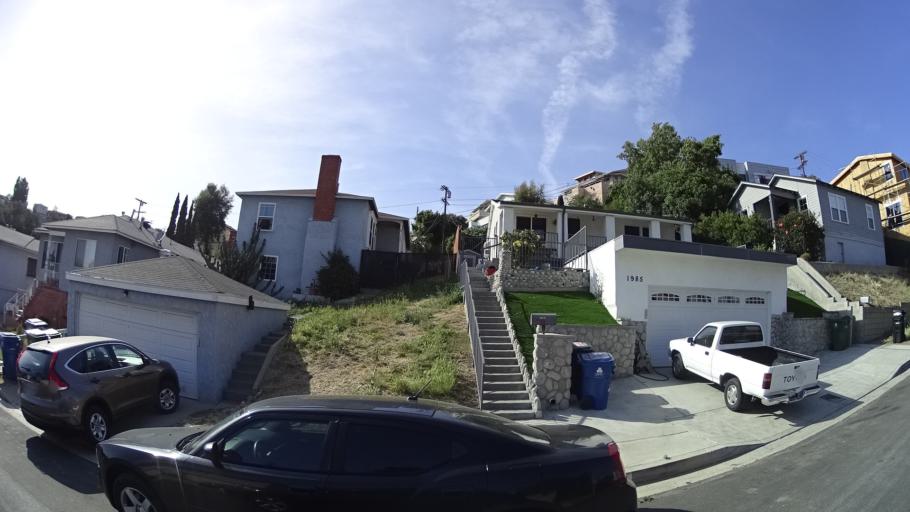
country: US
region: California
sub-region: Los Angeles County
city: Belvedere
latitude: 34.0662
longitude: -118.1728
